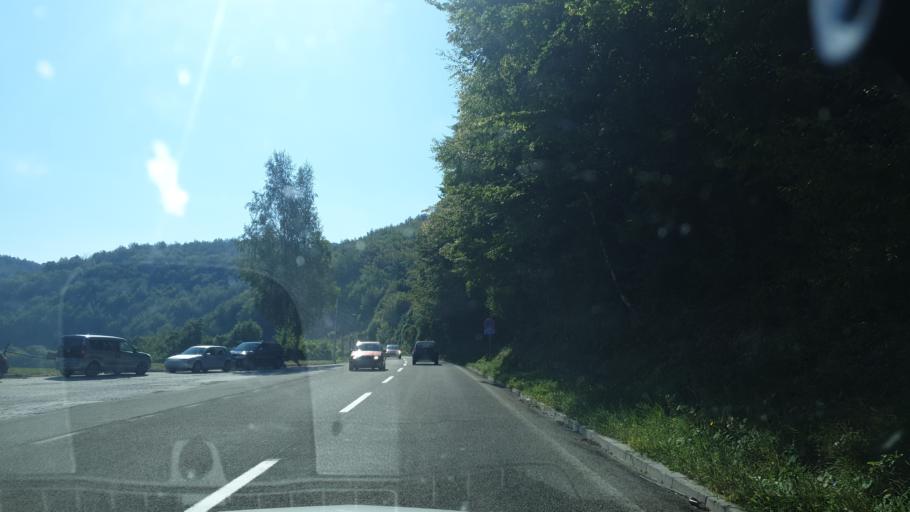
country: RS
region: Central Serbia
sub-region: Zlatiborski Okrug
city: Nova Varos
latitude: 43.5059
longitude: 19.8123
